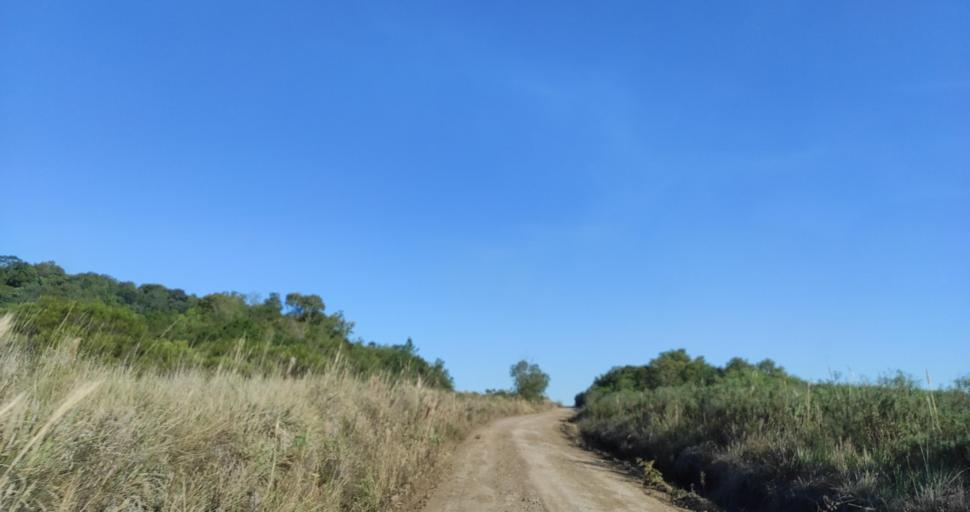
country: AR
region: Misiones
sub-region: Departamento de Apostoles
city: San Jose
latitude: -27.6673
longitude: -55.6603
